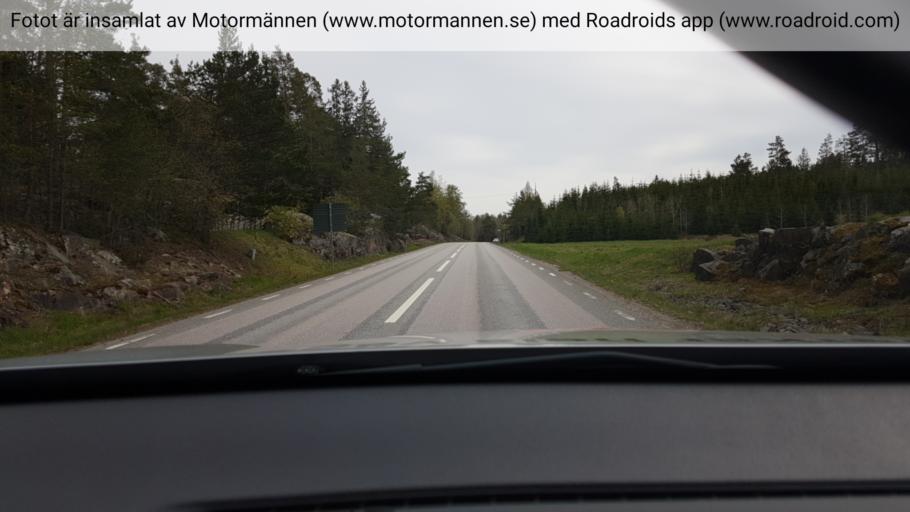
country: SE
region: Stockholm
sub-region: Norrtalje Kommun
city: Nykvarn
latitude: 59.9166
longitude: 18.1010
